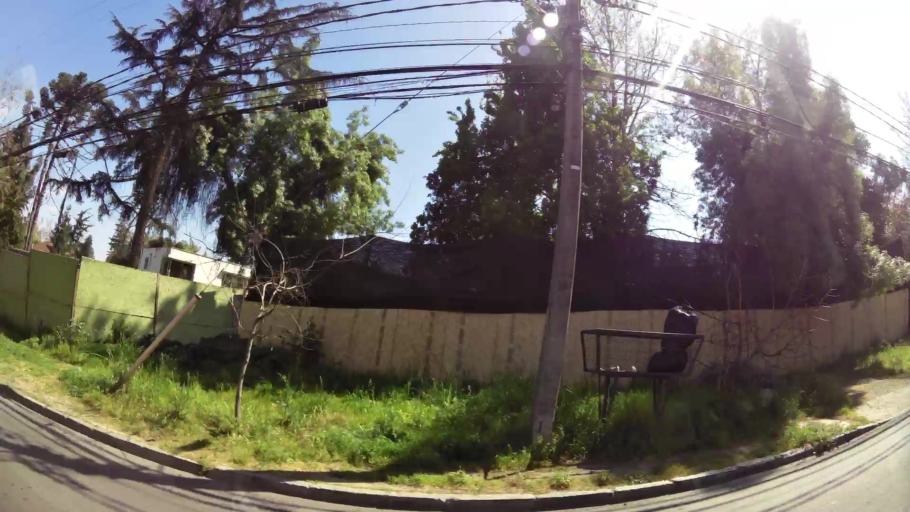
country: CL
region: Santiago Metropolitan
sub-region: Provincia de Santiago
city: Villa Presidente Frei, Nunoa, Santiago, Chile
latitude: -33.4345
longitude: -70.5212
